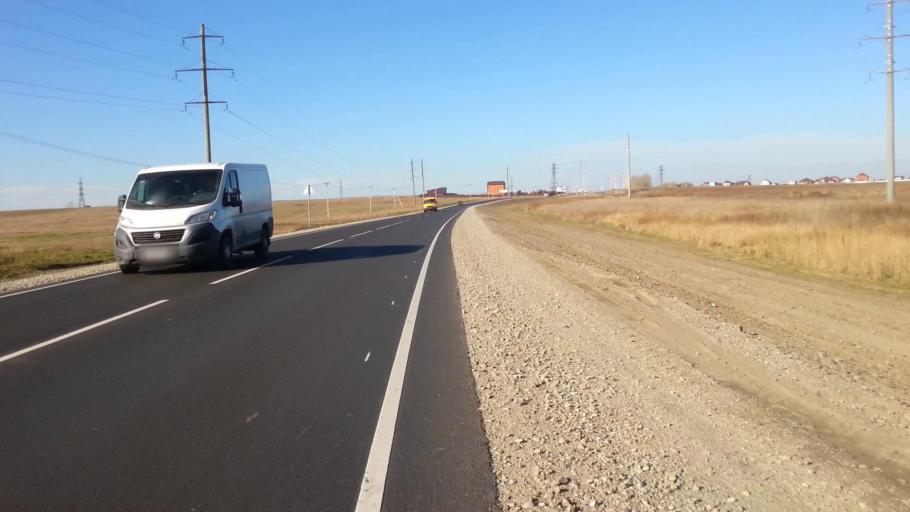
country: RU
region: Altai Krai
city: Sannikovo
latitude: 53.3304
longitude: 83.9384
